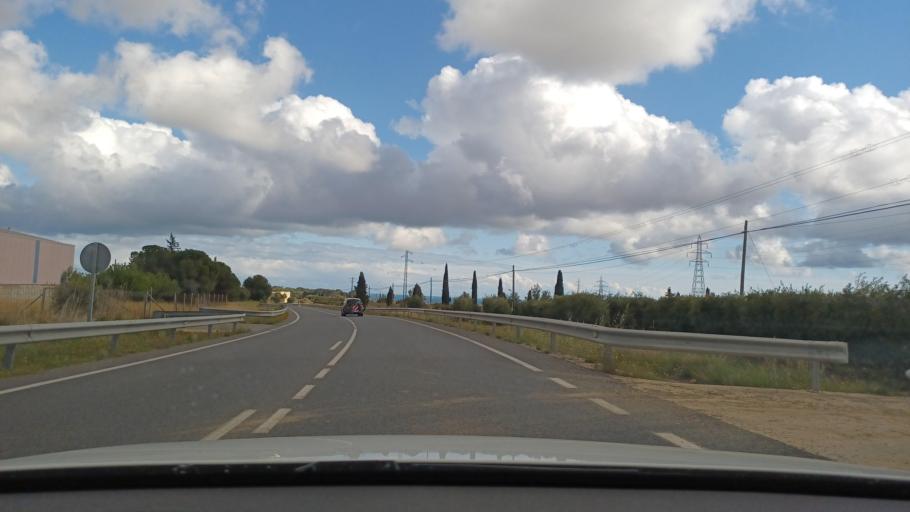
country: ES
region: Catalonia
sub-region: Provincia de Tarragona
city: Botarell
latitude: 41.1137
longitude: 1.0115
